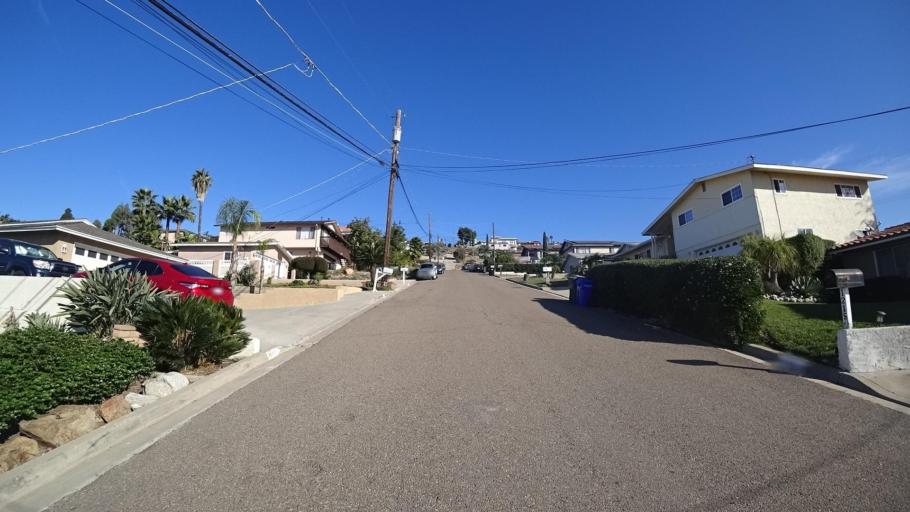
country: US
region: California
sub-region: San Diego County
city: La Presa
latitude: 32.7172
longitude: -116.9943
